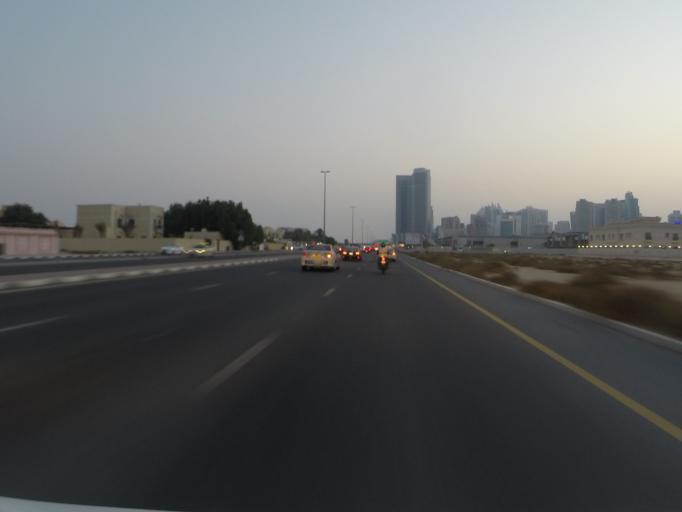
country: AE
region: Dubai
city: Dubai
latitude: 25.1028
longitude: 55.1867
